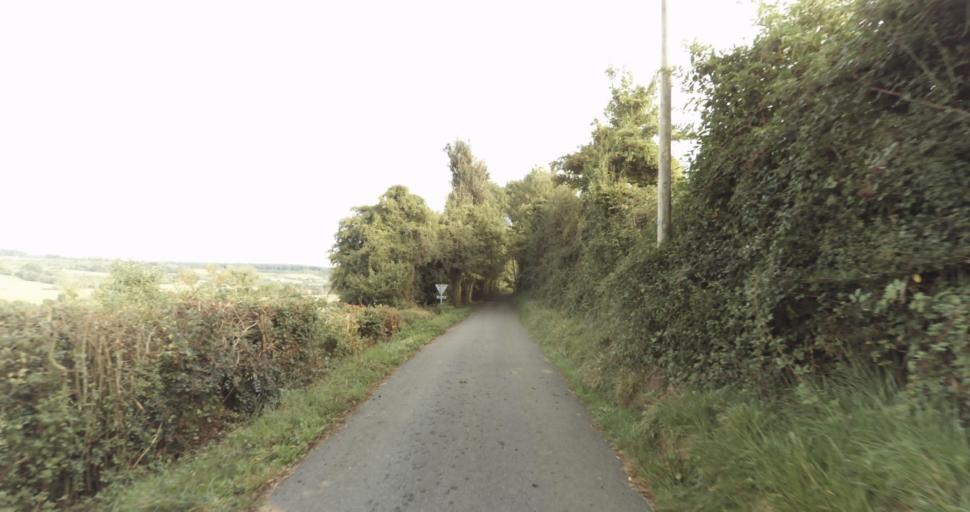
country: FR
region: Lower Normandy
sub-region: Departement de l'Orne
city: Vimoutiers
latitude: 48.8784
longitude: 0.2258
